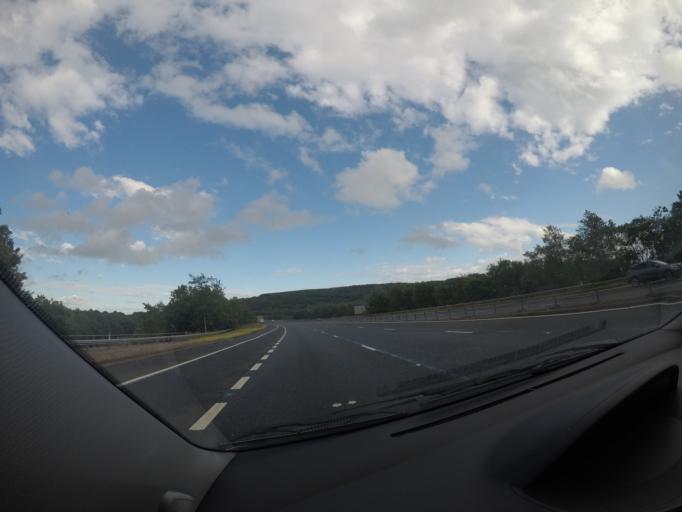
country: GB
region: Scotland
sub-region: Dumfries and Galloway
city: Annan
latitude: 55.0586
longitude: -3.2552
